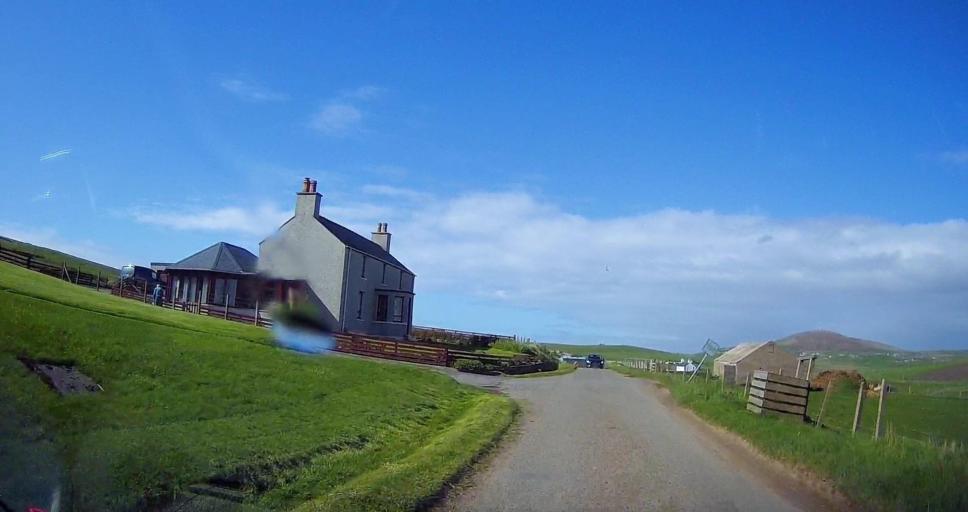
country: GB
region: Scotland
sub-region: Shetland Islands
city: Sandwick
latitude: 59.9084
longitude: -1.3344
